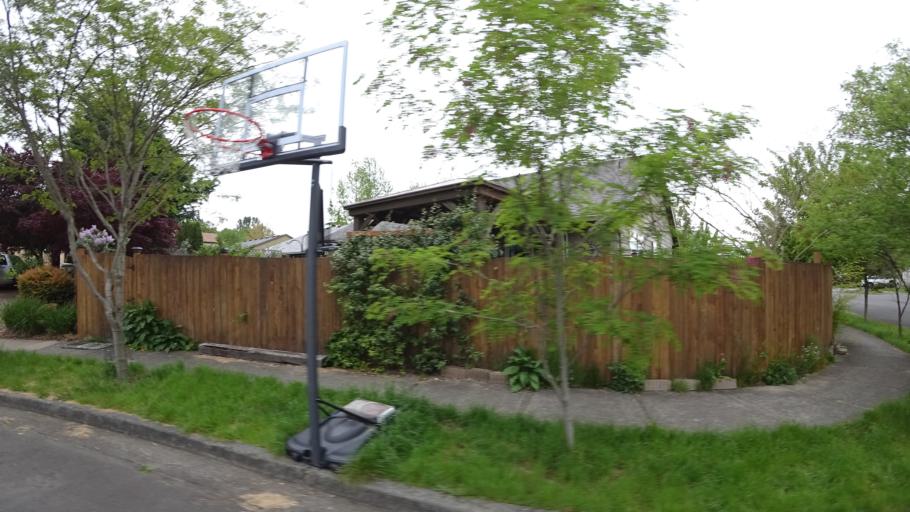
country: US
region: Oregon
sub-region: Washington County
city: Aloha
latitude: 45.5131
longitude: -122.9129
